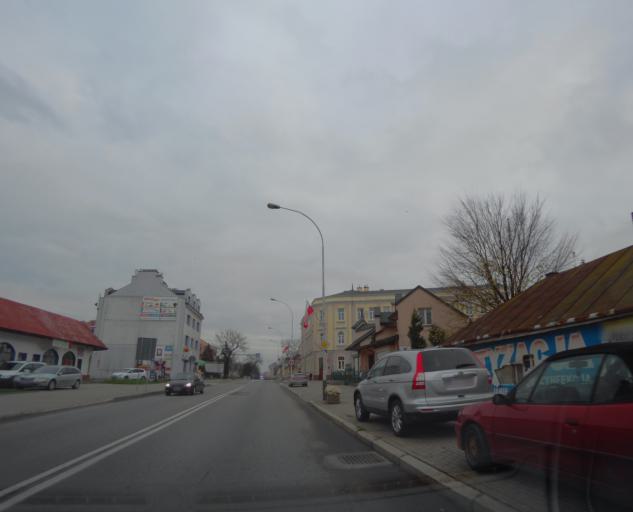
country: PL
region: Subcarpathian Voivodeship
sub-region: Powiat jaroslawski
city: Jaroslaw
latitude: 50.0159
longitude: 22.6885
